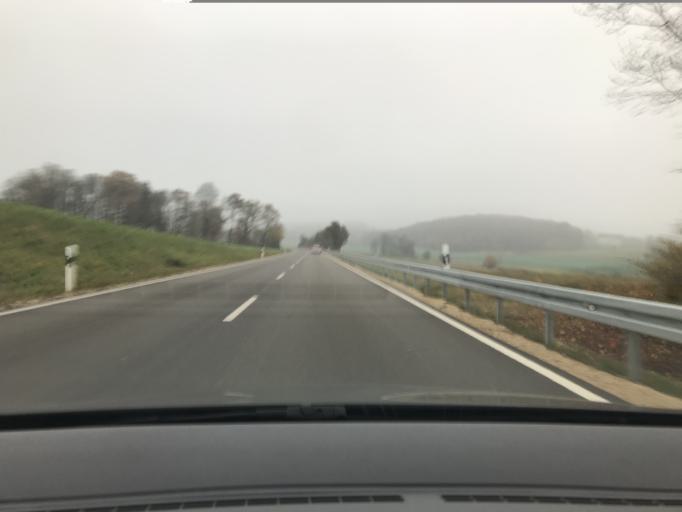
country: DE
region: Bavaria
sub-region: Swabia
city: Fremdingen
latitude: 48.9803
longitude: 10.4420
